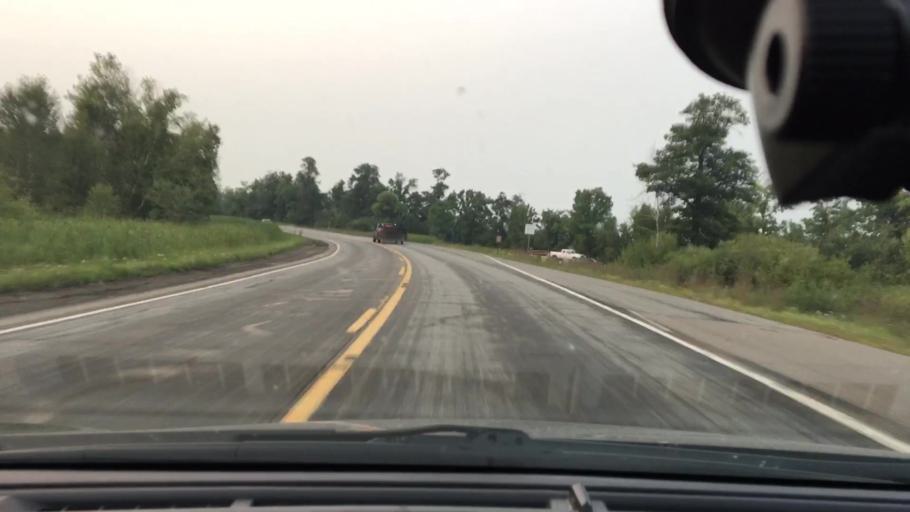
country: US
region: Minnesota
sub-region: Crow Wing County
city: Cross Lake
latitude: 46.7161
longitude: -93.9539
